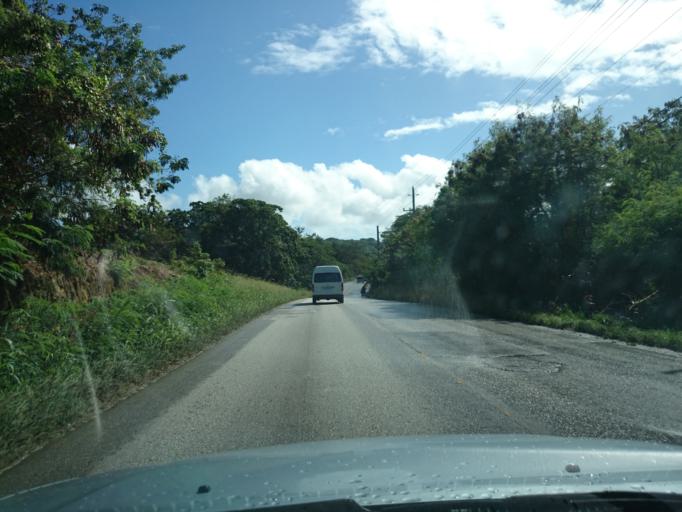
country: BB
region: Saint James
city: Holetown
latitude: 13.1899
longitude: -59.6116
